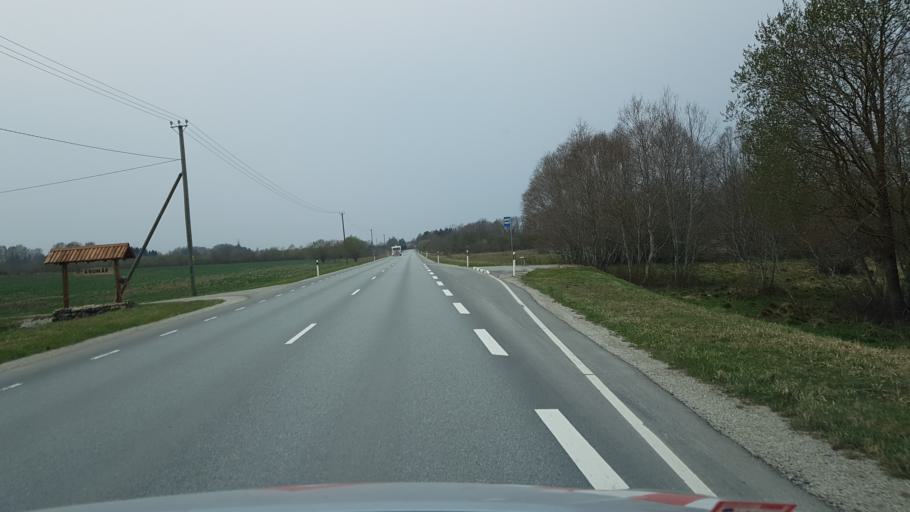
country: EE
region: Harju
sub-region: Joelaehtme vald
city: Loo
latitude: 59.3909
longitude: 24.9794
